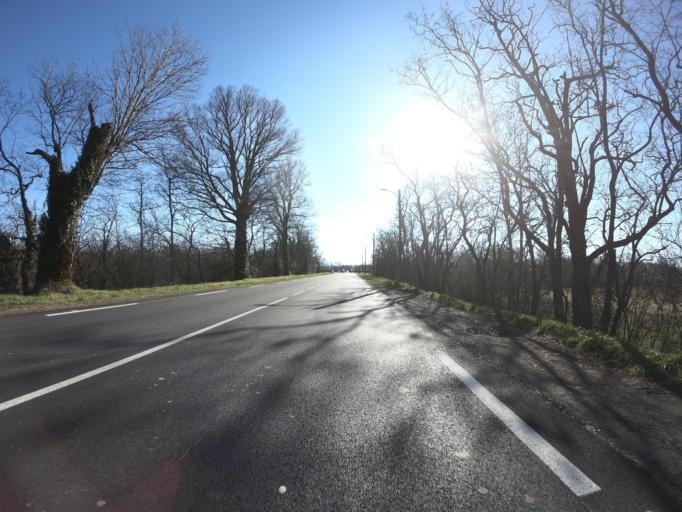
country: FR
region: Midi-Pyrenees
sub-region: Departement de l'Ariege
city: Mirepoix
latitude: 43.0956
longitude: 1.8762
